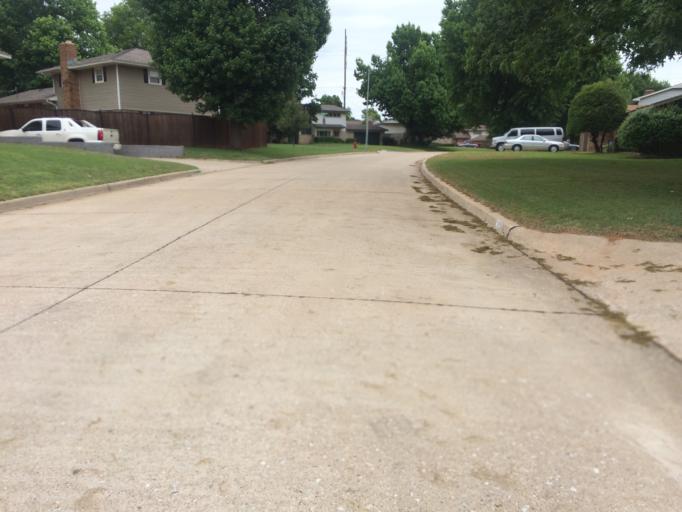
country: US
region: Oklahoma
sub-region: Cleveland County
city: Norman
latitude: 35.2100
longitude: -97.4793
